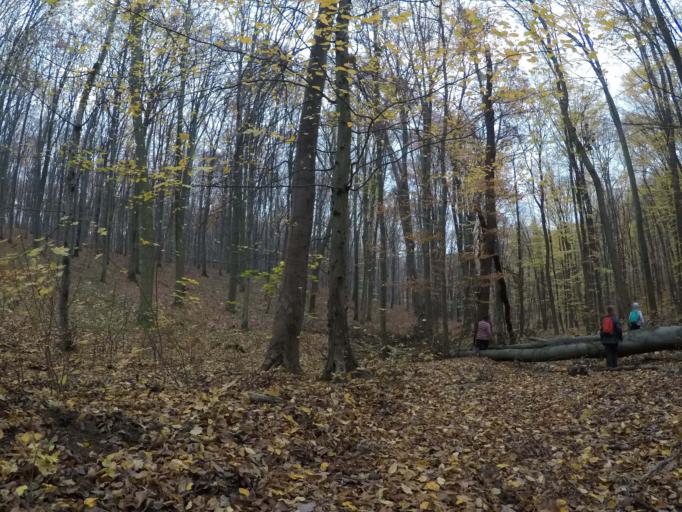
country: SK
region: Presovsky
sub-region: Okres Presov
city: Presov
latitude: 48.9673
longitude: 21.2038
